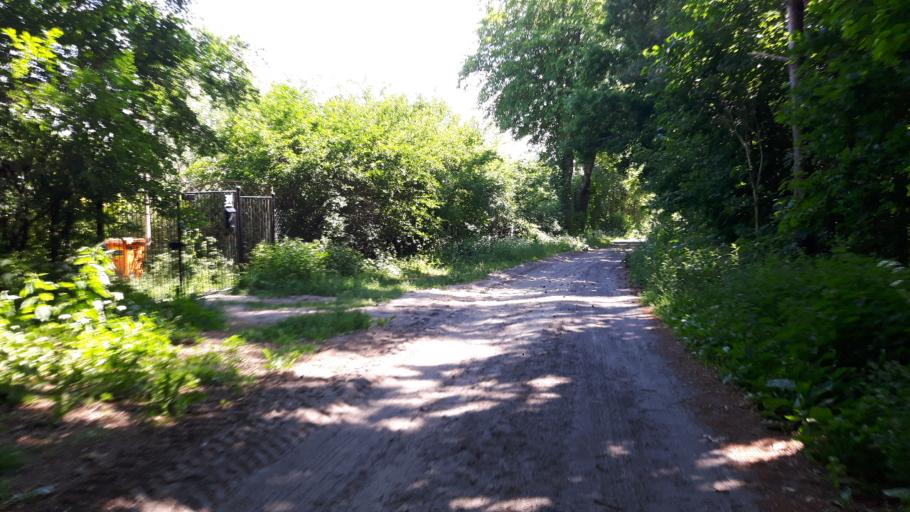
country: PL
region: Pomeranian Voivodeship
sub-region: Powiat wejherowski
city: Choczewo
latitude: 54.7315
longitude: 17.9541
